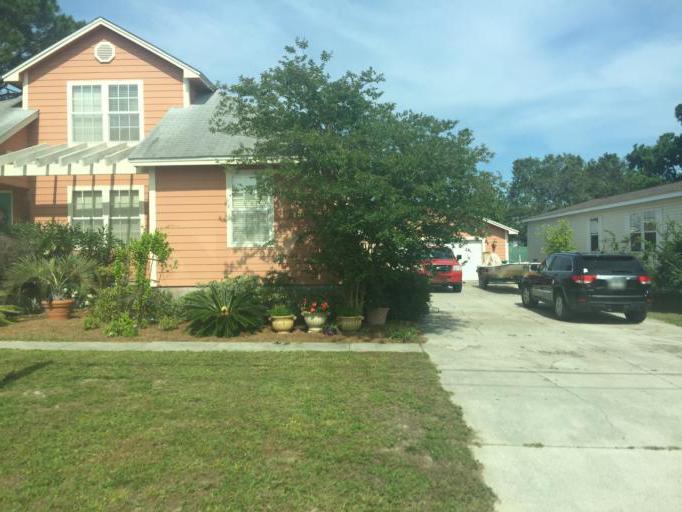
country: US
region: Florida
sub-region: Bay County
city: Laguna Beach
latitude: 30.2515
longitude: -85.9409
